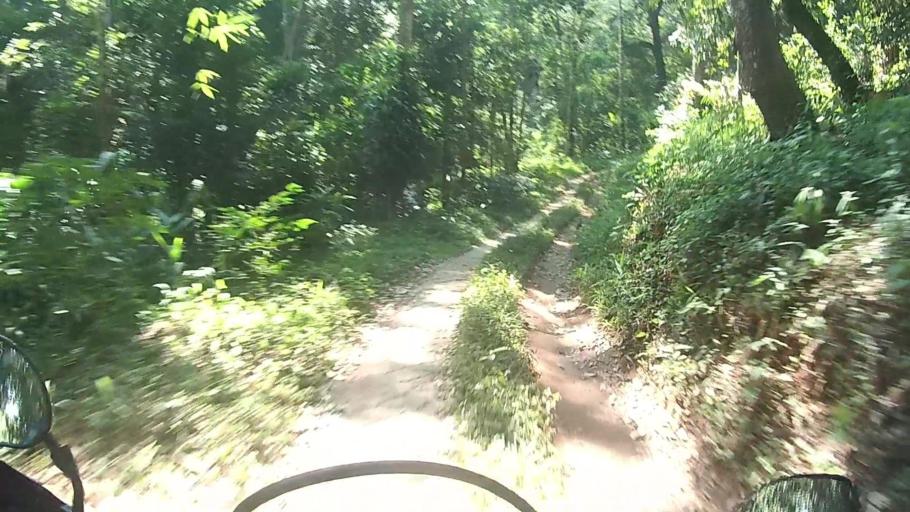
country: TH
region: Chiang Mai
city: Mae On
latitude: 19.0589
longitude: 99.3330
